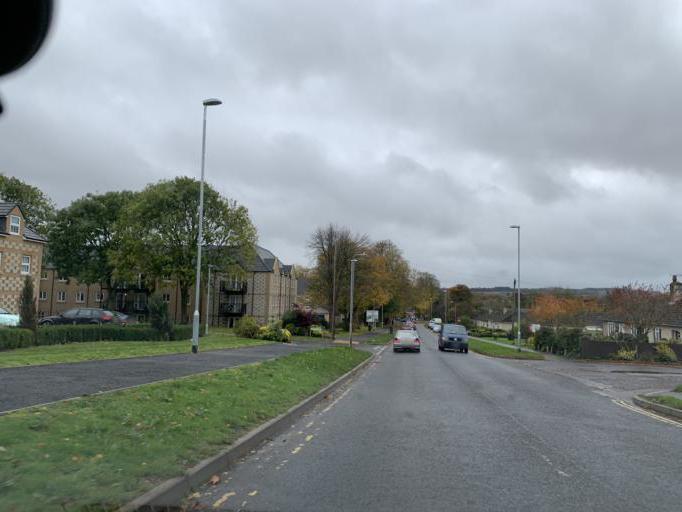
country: GB
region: England
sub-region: Wiltshire
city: Wilton
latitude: 51.0838
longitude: -1.8544
